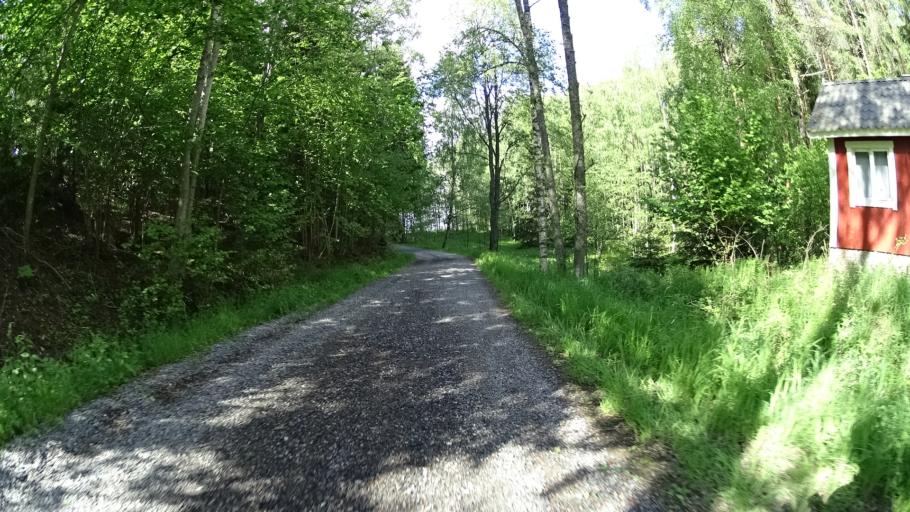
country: FI
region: Varsinais-Suomi
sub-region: Salo
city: Kisko
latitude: 60.1975
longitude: 23.5480
